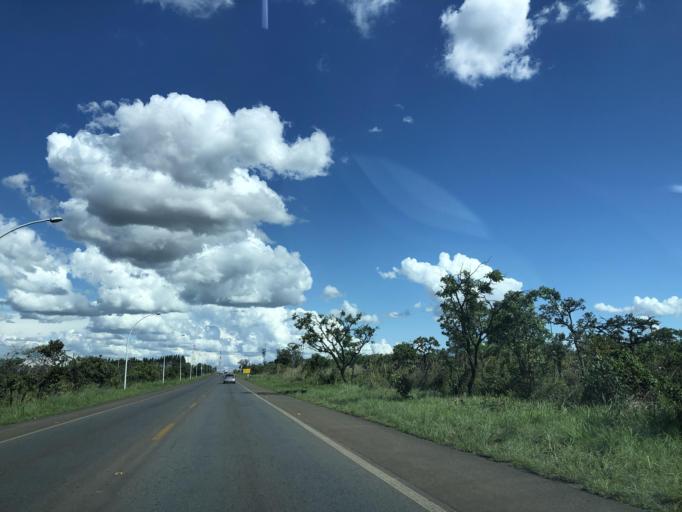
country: BR
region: Federal District
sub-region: Brasilia
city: Brasilia
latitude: -15.6792
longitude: -47.8704
